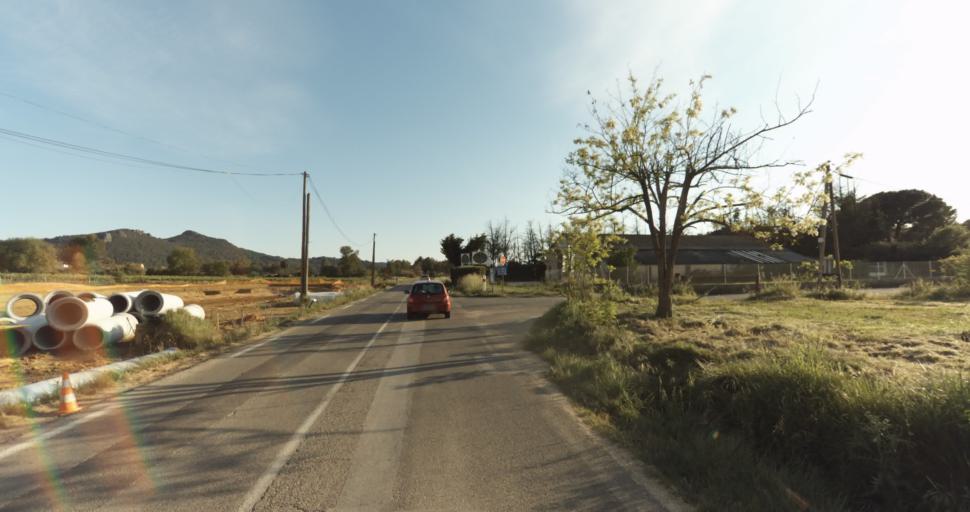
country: FR
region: Provence-Alpes-Cote d'Azur
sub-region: Departement du Var
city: La Crau
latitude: 43.1603
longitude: 6.0984
